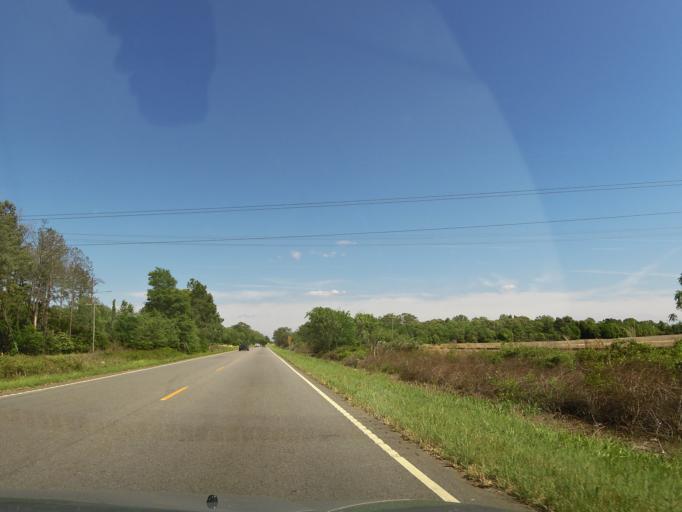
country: US
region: South Carolina
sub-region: Aiken County
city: Aiken
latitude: 33.5393
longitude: -81.6594
